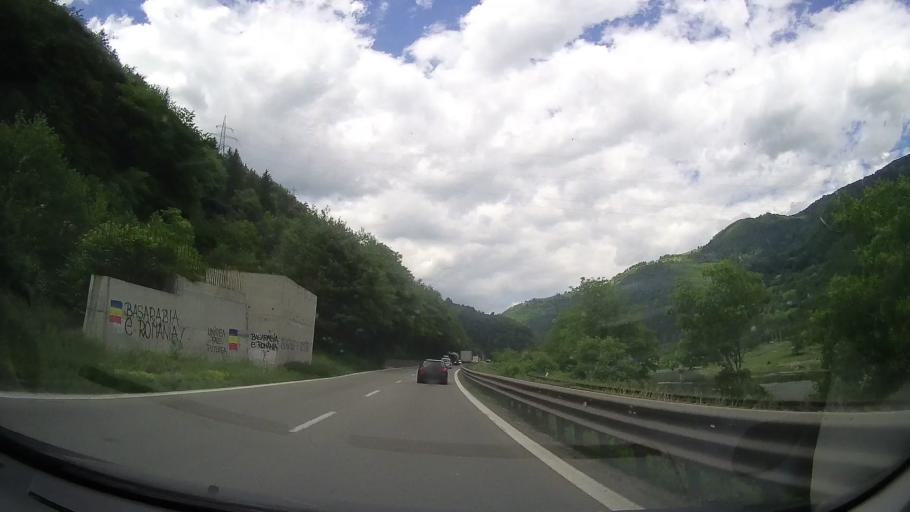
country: RO
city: Cainenii Mici
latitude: 45.5049
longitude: 24.2841
